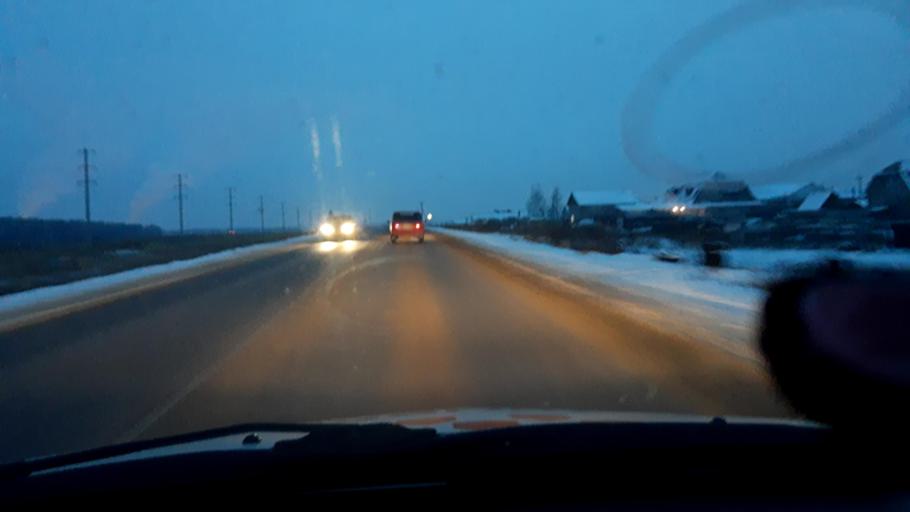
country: RU
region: Bashkortostan
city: Iglino
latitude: 54.7937
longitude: 56.2514
